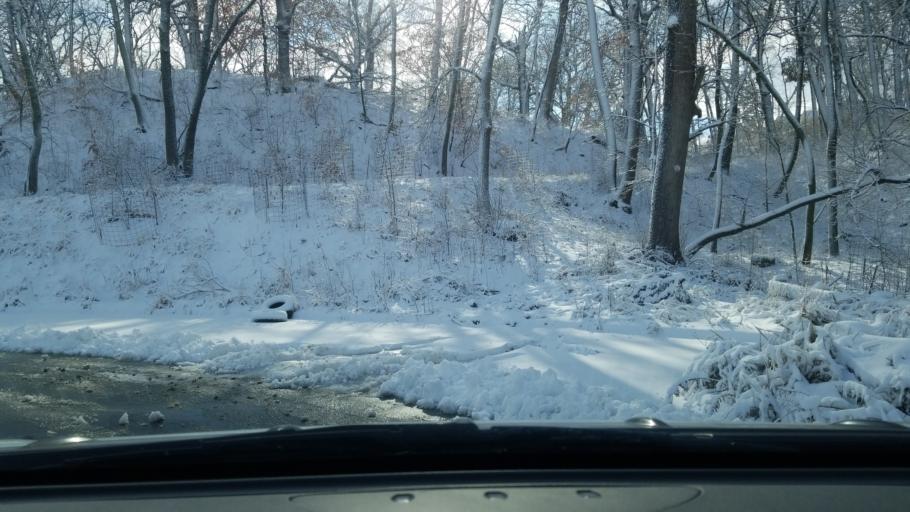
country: US
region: Nebraska
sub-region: Douglas County
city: Omaha
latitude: 41.2213
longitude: -95.9424
